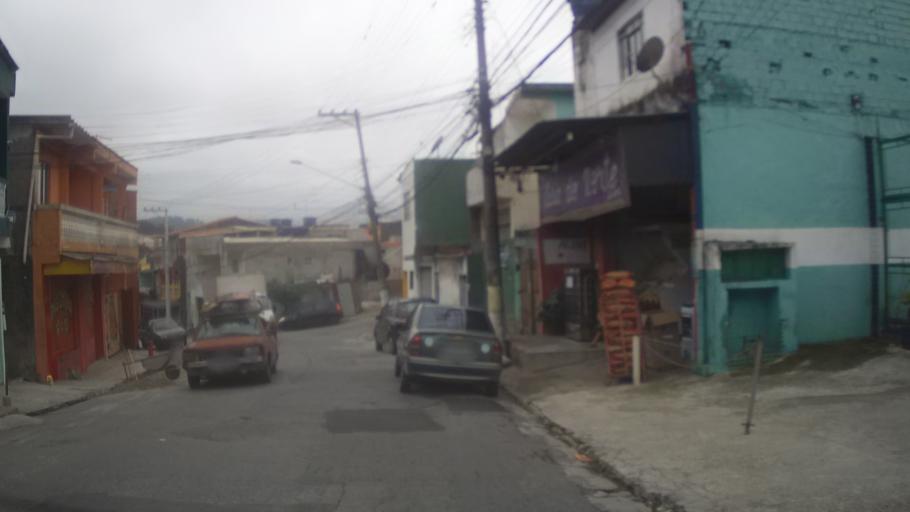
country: BR
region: Sao Paulo
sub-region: Guarulhos
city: Guarulhos
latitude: -23.4272
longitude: -46.5129
